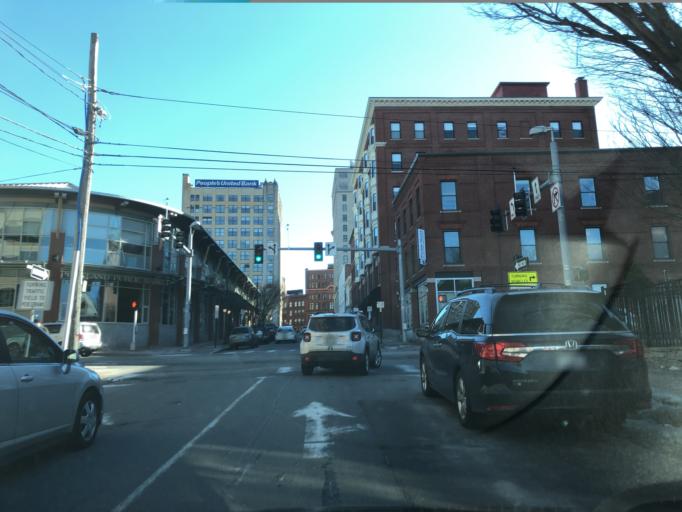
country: US
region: Maine
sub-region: Cumberland County
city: Portland
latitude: 43.6586
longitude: -70.2612
